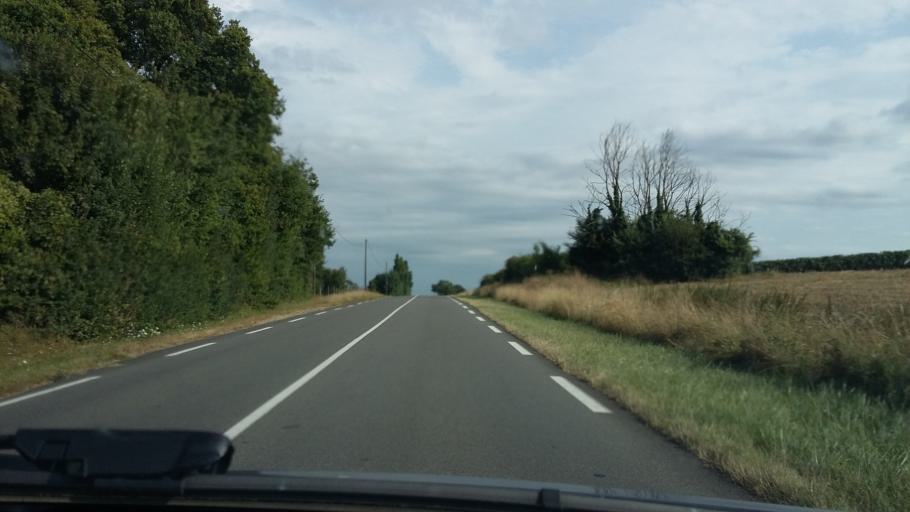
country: FR
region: Poitou-Charentes
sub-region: Departement de la Charente
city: Asnieres-sur-Nouere
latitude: 45.7153
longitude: 0.0745
